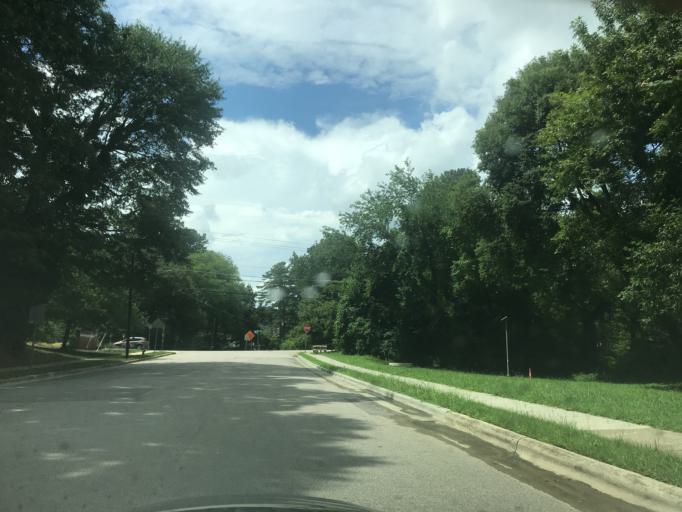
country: US
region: North Carolina
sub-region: Wake County
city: West Raleigh
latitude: 35.8203
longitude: -78.6339
